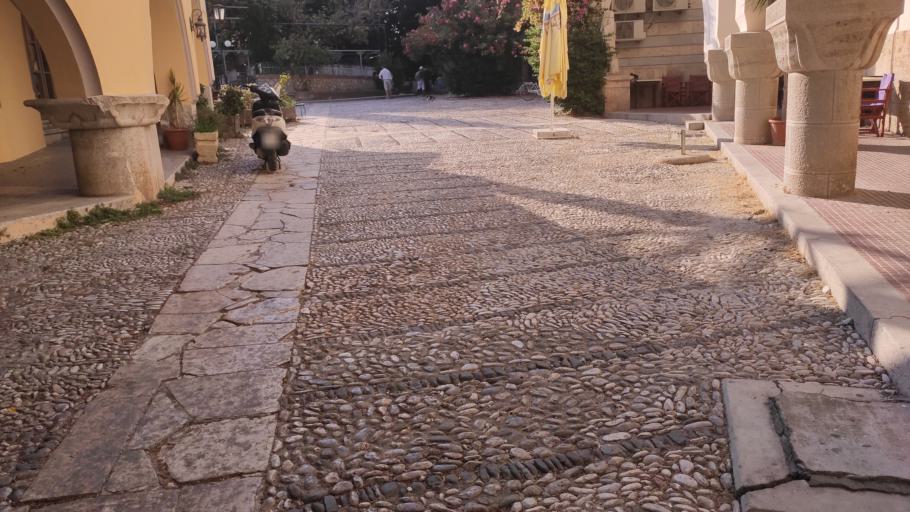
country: GR
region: South Aegean
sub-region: Nomos Dodekanisou
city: Kos
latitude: 36.8946
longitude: 27.2915
